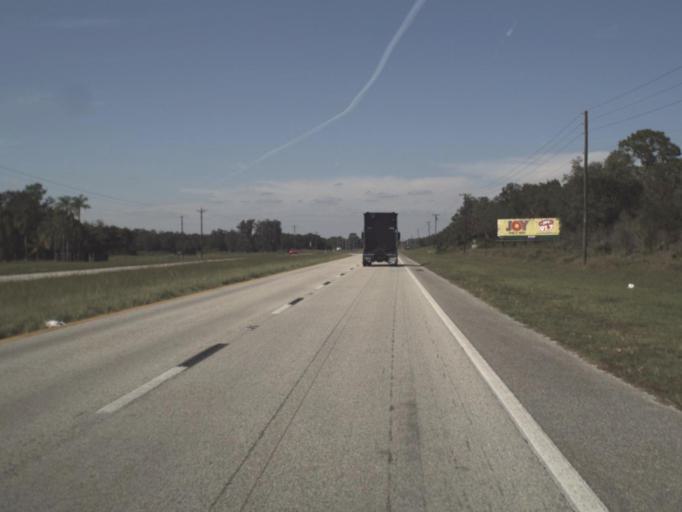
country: US
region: Florida
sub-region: Highlands County
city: Lake Placid
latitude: 27.3843
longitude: -81.4092
